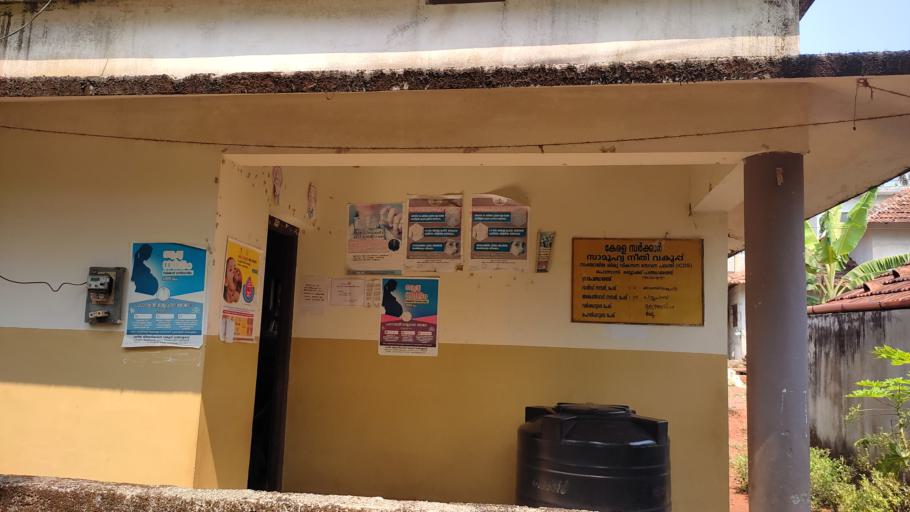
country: IN
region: Kerala
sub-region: Malappuram
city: Ponnani
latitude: 10.8308
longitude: 76.0136
